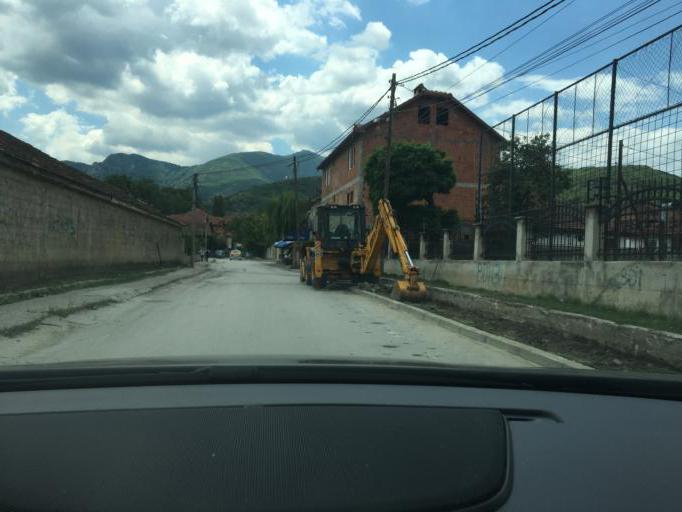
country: MK
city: Ljubin
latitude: 41.9812
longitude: 21.3070
